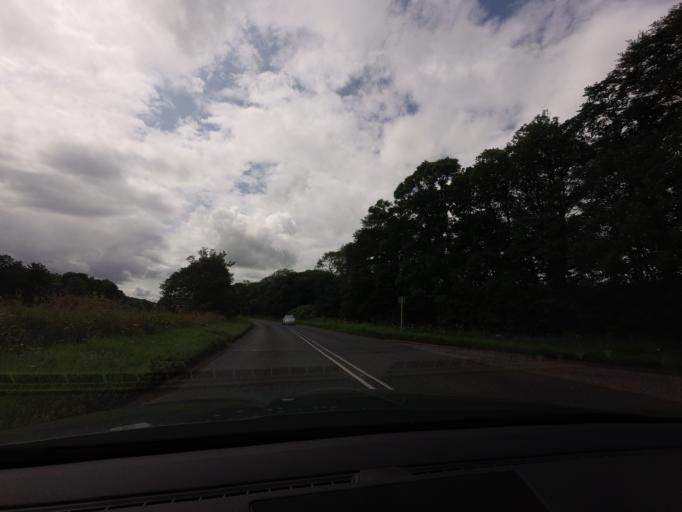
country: GB
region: Scotland
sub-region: Aberdeenshire
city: Whitehills
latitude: 57.6646
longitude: -2.5752
